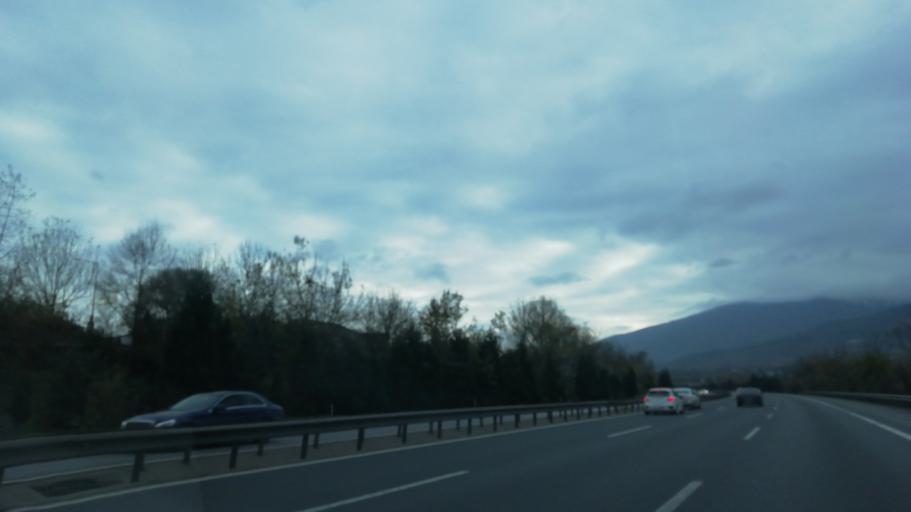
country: TR
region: Kocaeli
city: Derbent
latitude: 40.7176
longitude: 30.1112
